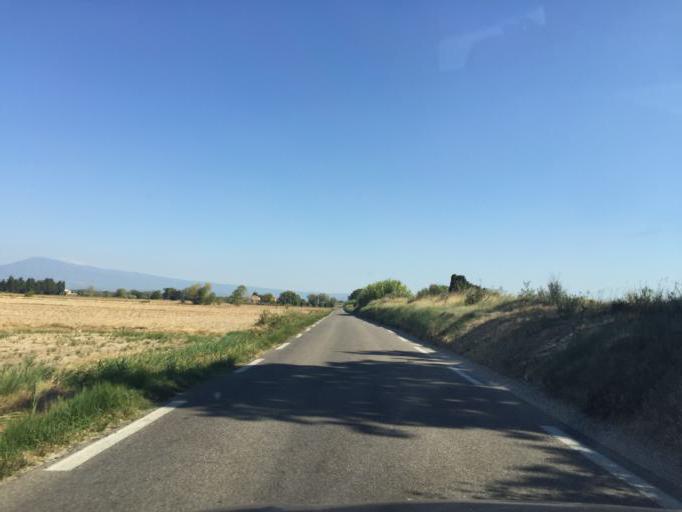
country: FR
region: Provence-Alpes-Cote d'Azur
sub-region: Departement du Vaucluse
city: Bedarrides
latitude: 44.0318
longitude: 4.9285
